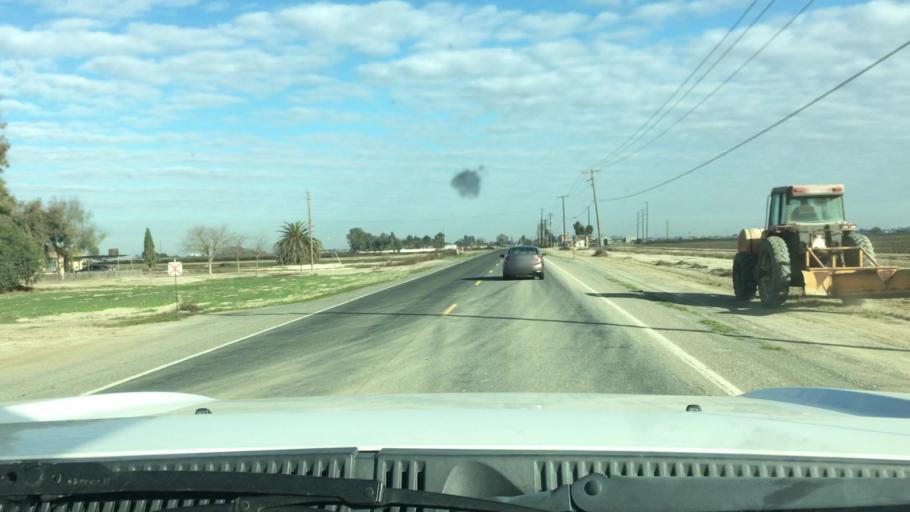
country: US
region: California
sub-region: Kings County
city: Stratford
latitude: 36.2189
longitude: -119.7803
